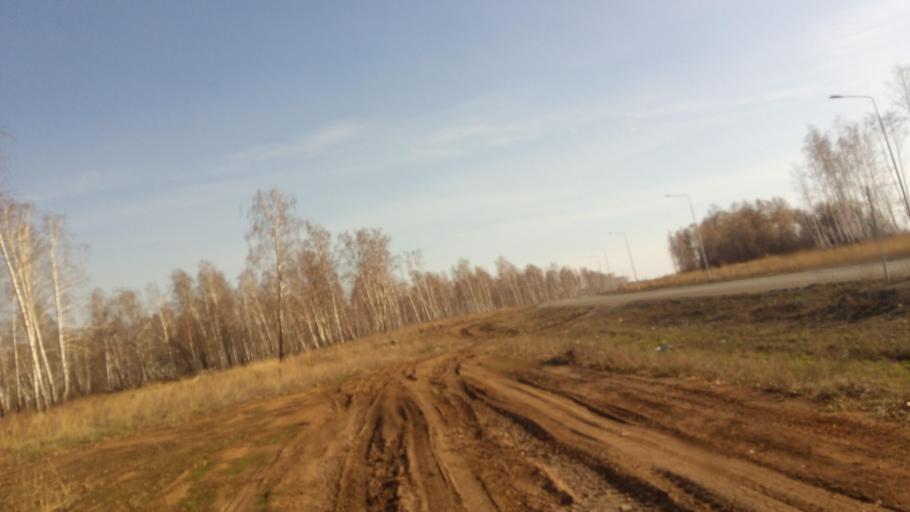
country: RU
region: Chelyabinsk
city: Sargazy
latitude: 55.1147
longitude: 61.2361
